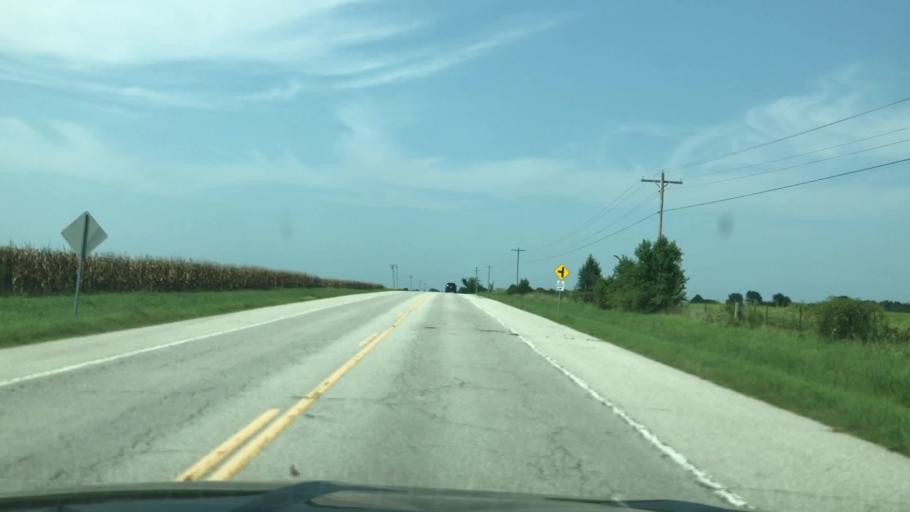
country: US
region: Oklahoma
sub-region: Ottawa County
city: Commerce
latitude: 36.9265
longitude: -94.8419
